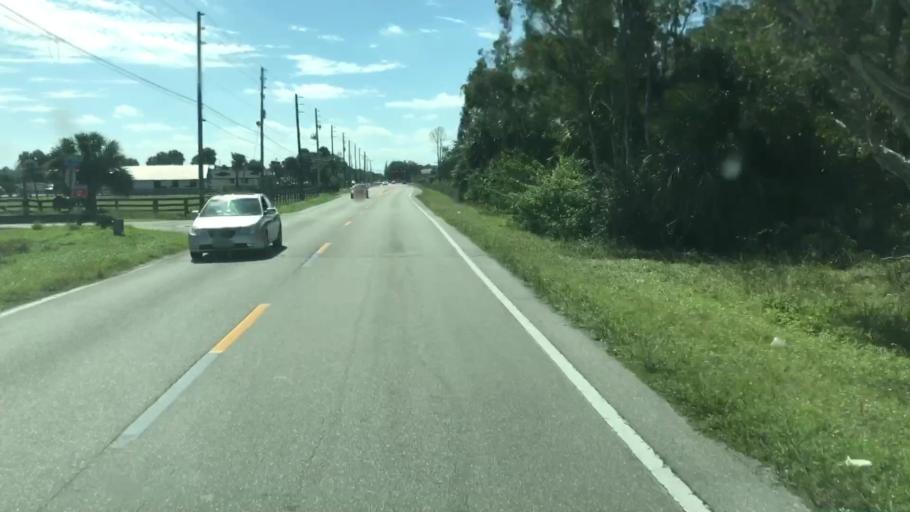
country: US
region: Florida
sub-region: Lee County
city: Bonita Springs
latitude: 26.3355
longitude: -81.7386
